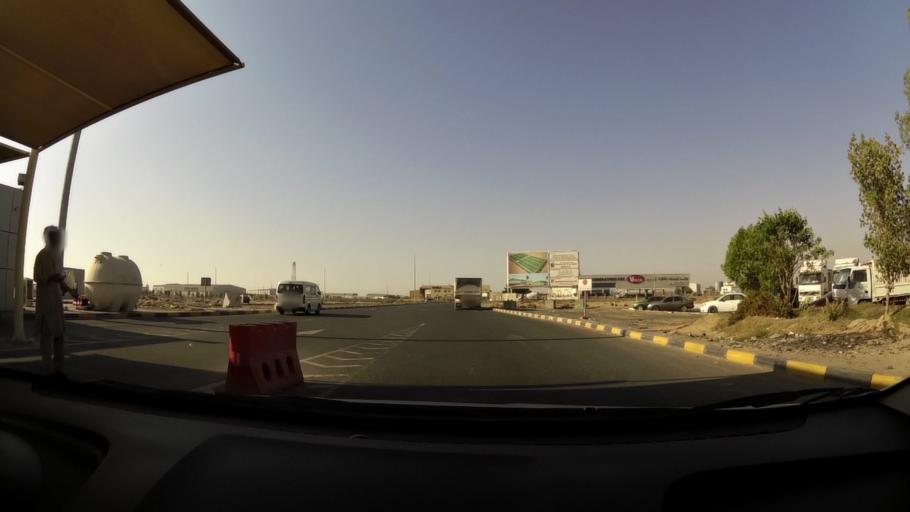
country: AE
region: Ajman
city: Ajman
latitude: 25.4431
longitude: 55.5497
